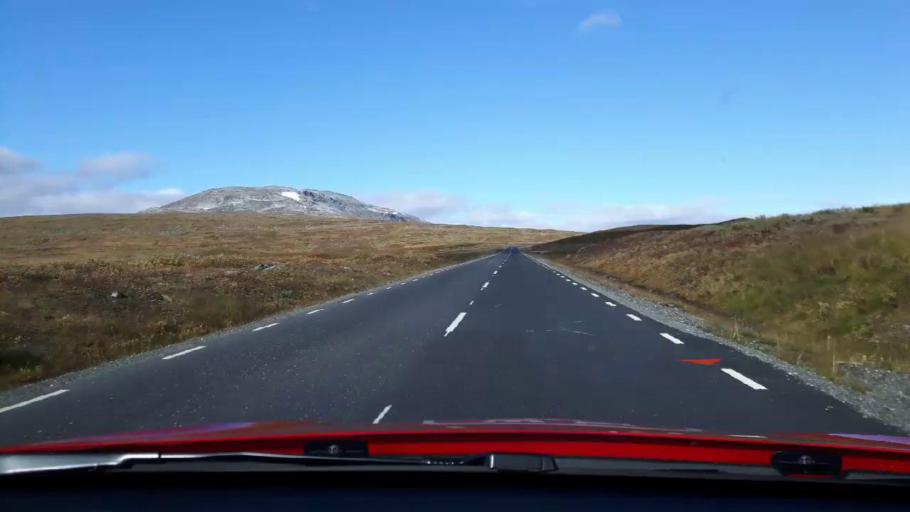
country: NO
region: Nordland
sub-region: Hattfjelldal
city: Hattfjelldal
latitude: 65.0331
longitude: 14.3342
